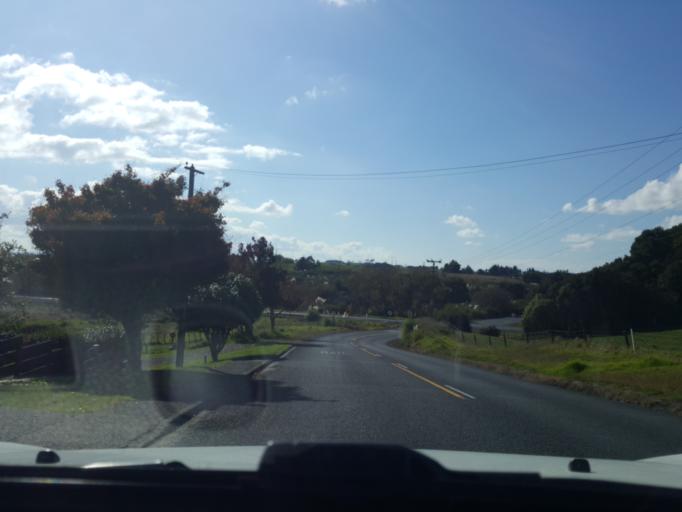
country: NZ
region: Waikato
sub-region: Waikato District
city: Ngaruawahia
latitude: -37.5412
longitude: 175.1735
